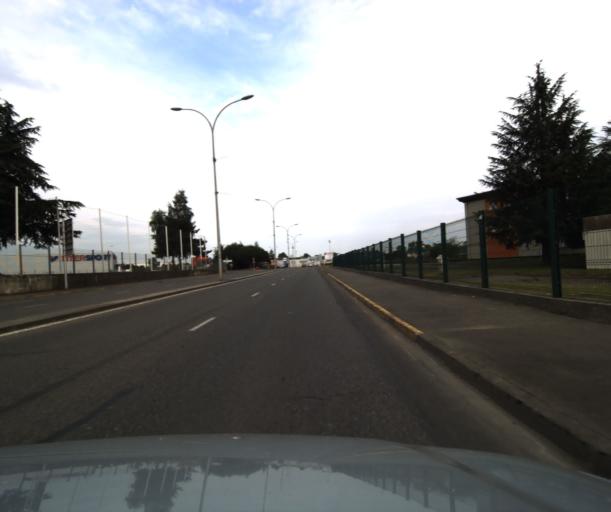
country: FR
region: Midi-Pyrenees
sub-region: Departement des Hautes-Pyrenees
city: Tarbes
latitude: 43.2191
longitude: 0.0825
